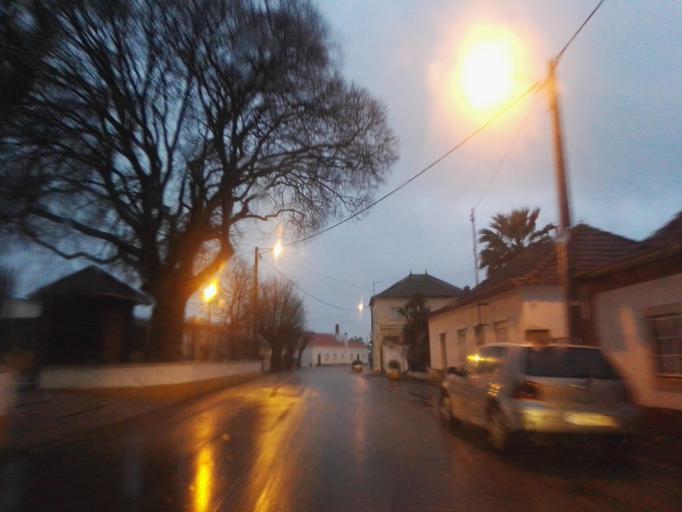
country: PT
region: Santarem
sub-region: Santarem
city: Alcanede
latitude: 39.3146
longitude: -8.7820
